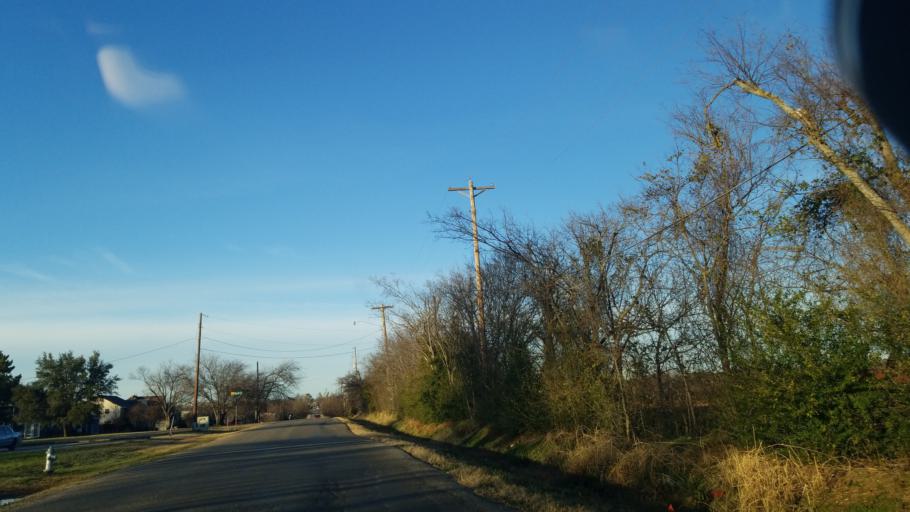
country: US
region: Texas
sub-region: Denton County
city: Denton
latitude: 33.1890
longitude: -97.1617
